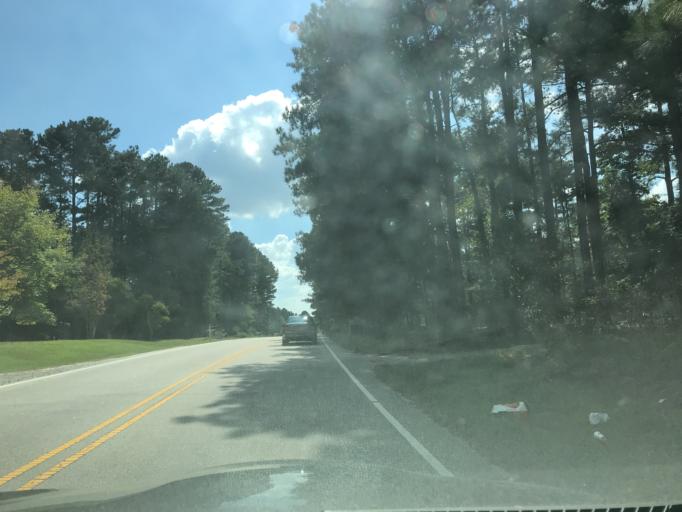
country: US
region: North Carolina
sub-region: Wake County
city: Rolesville
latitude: 35.8954
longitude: -78.5240
